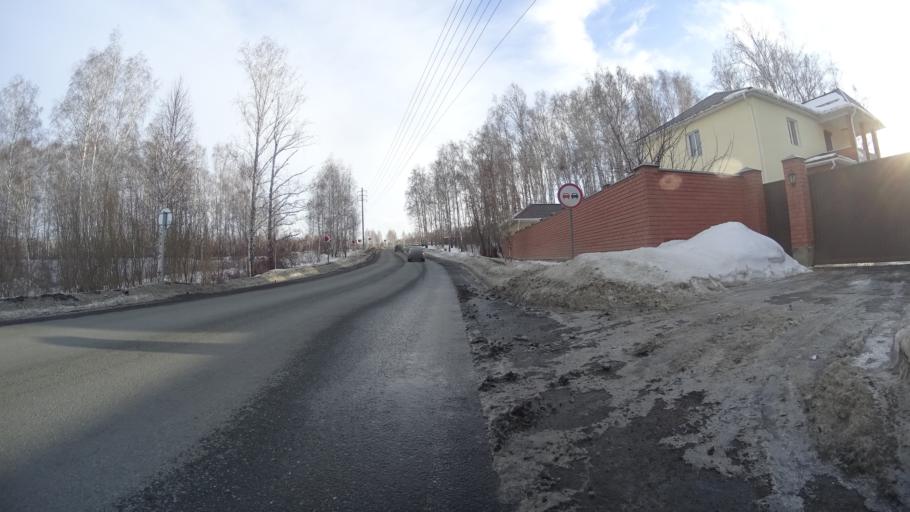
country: RU
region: Chelyabinsk
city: Sargazy
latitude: 55.1293
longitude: 61.2881
